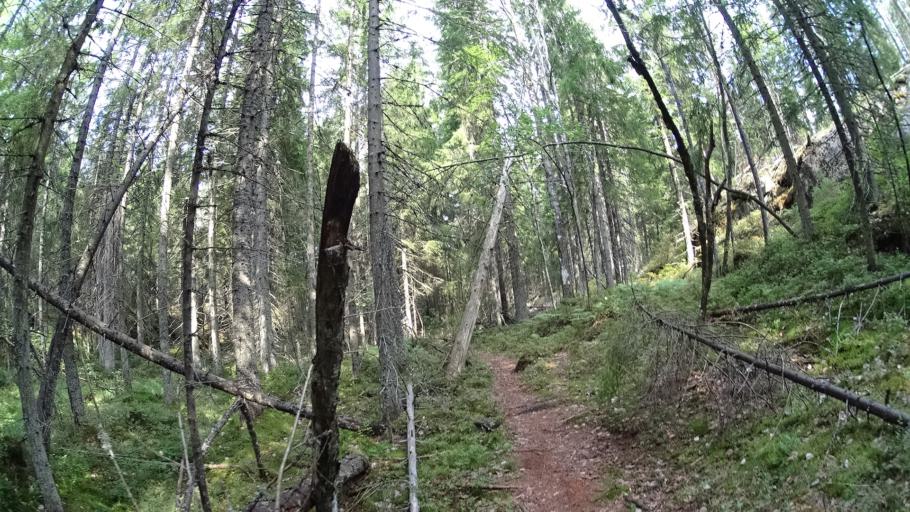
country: FI
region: Uusimaa
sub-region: Helsinki
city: Espoo
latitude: 60.3014
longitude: 24.5866
